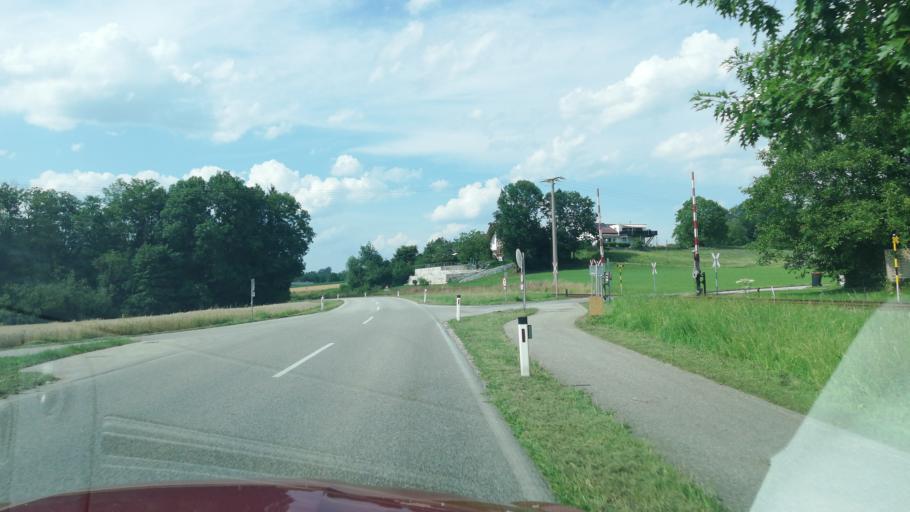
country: AT
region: Upper Austria
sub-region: Politischer Bezirk Vocklabruck
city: Puhret
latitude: 48.0301
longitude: 13.7041
